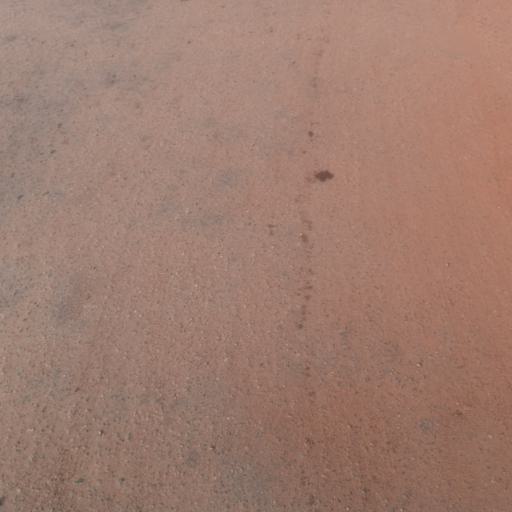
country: NG
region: Ondo
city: Ilare
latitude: 7.2989
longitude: 5.1355
